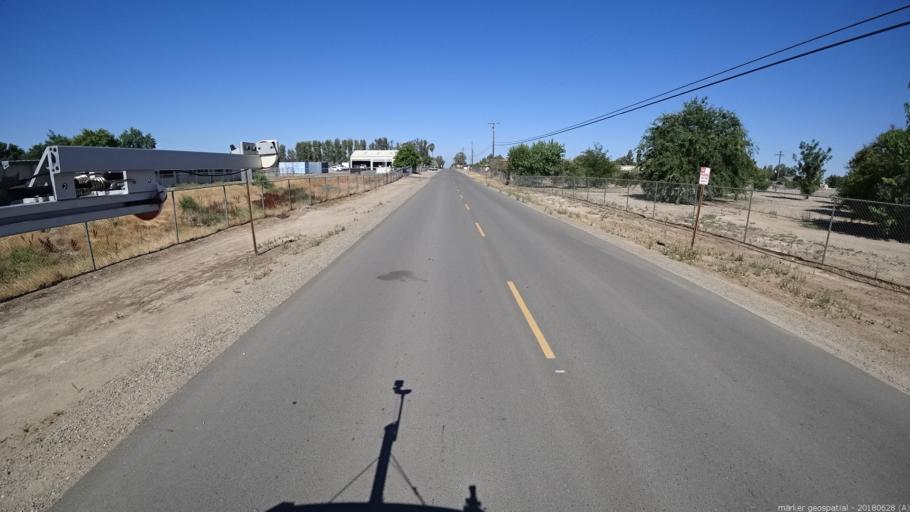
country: US
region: California
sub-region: Madera County
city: Bonadelle Ranchos-Madera Ranchos
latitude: 36.9885
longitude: -119.8803
